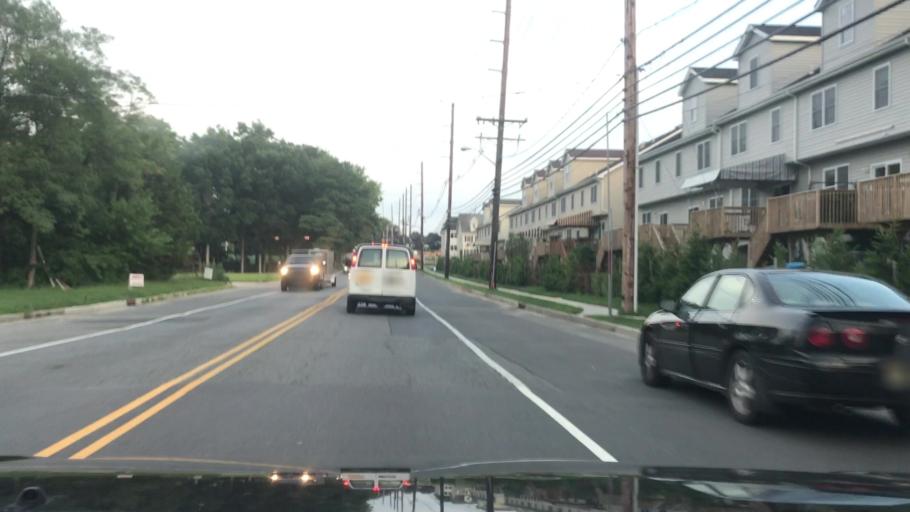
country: US
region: New Jersey
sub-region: Ocean County
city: Leisure Village
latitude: 40.0564
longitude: -74.2239
